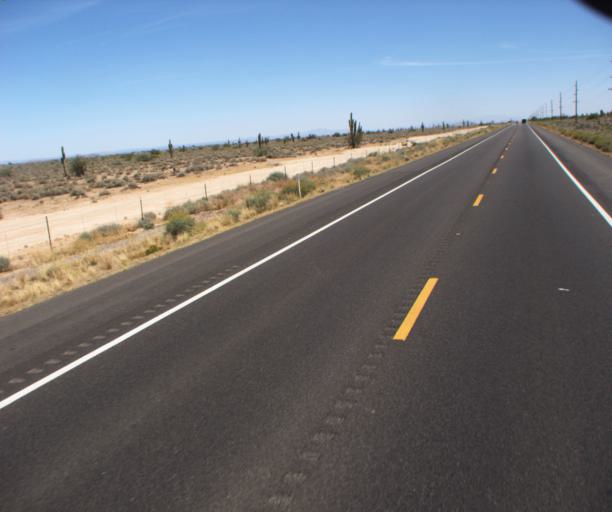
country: US
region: Arizona
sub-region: Pinal County
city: Blackwater
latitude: 33.0337
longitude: -111.6523
